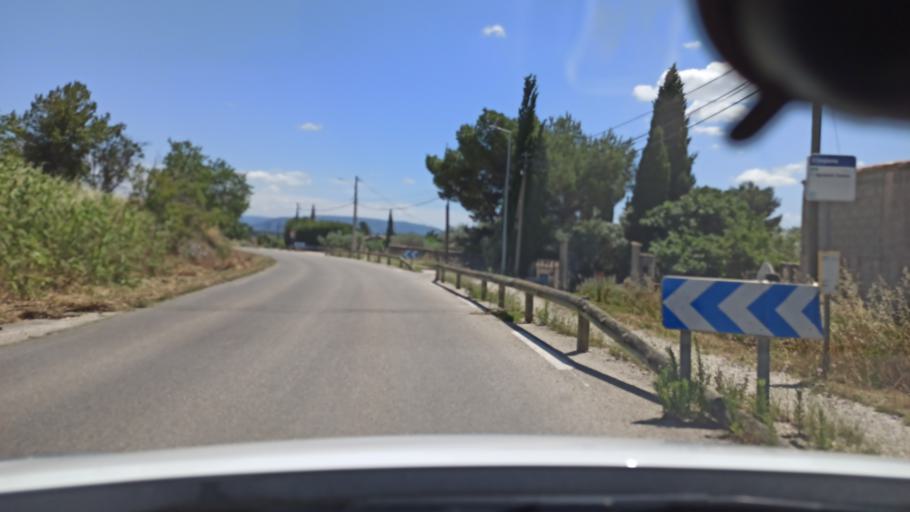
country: FR
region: Provence-Alpes-Cote d'Azur
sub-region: Departement du Vaucluse
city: Caumont-sur-Durance
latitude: 43.8963
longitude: 4.9402
